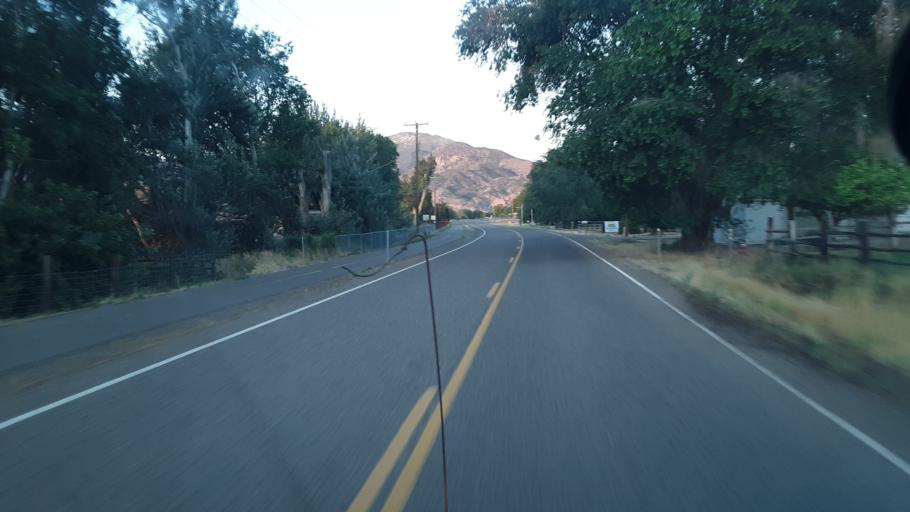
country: US
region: Utah
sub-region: Sevier County
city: Monroe
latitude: 38.5978
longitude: -112.2470
